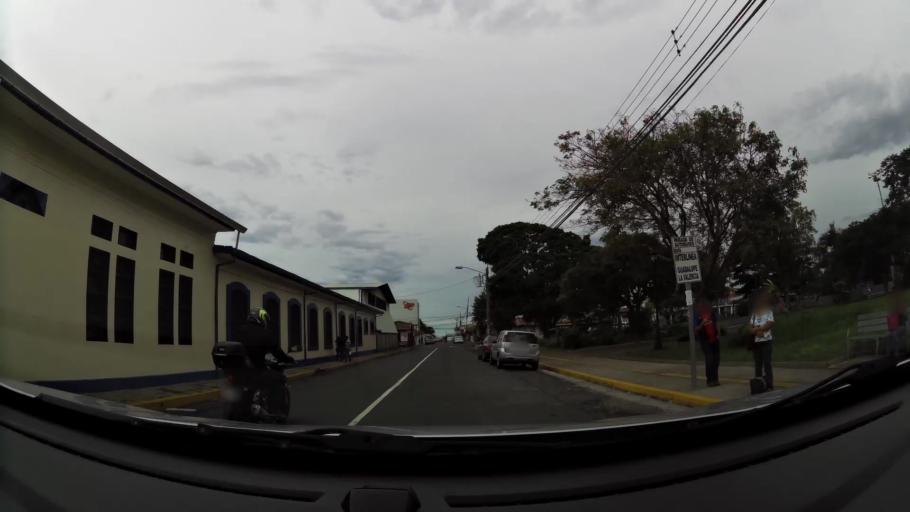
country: CR
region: San Jose
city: San Vicente de Moravia
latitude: 9.9612
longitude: -84.0490
